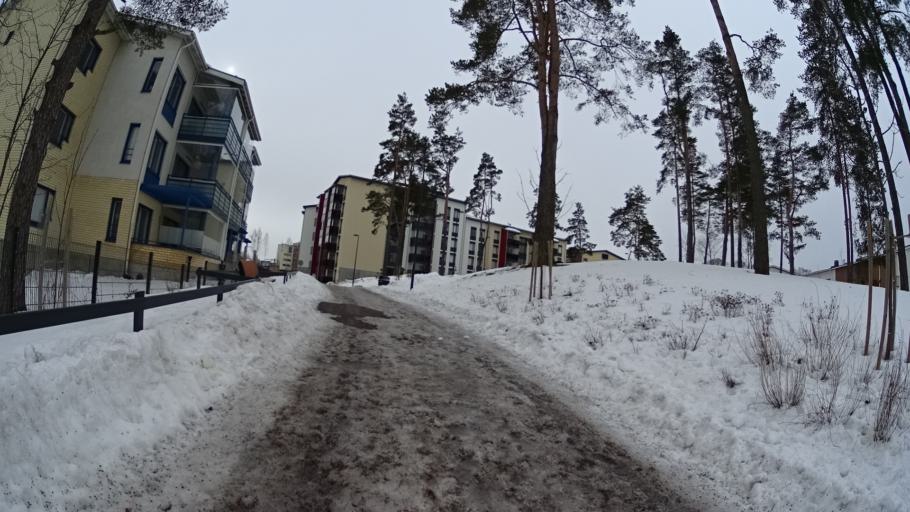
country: FI
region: Uusimaa
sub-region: Helsinki
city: Teekkarikylae
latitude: 60.2572
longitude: 24.8676
